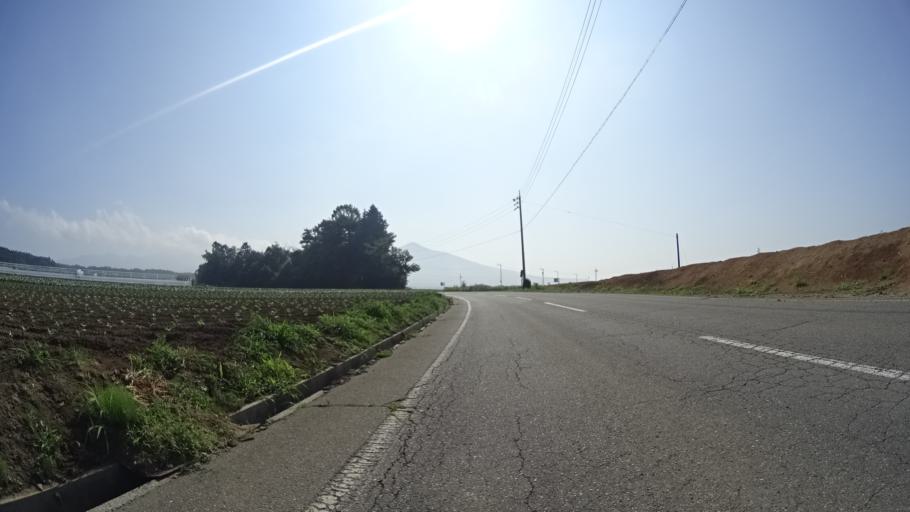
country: JP
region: Nagano
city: Chino
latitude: 35.9440
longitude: 138.2459
